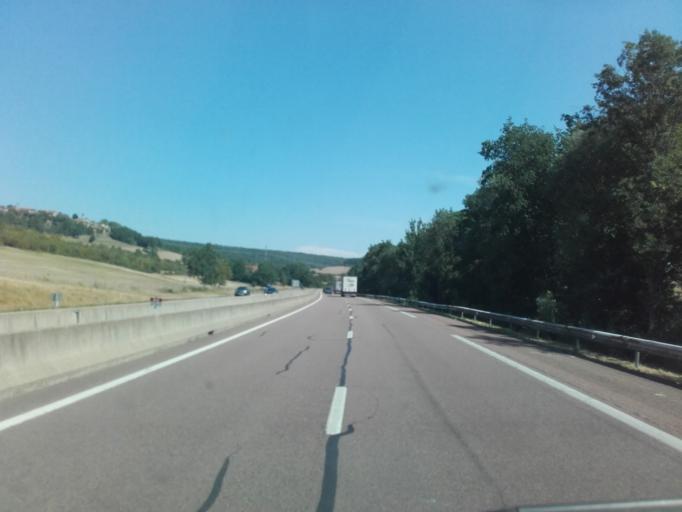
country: FR
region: Bourgogne
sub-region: Departement de la Cote-d'Or
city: Pouilly-en-Auxois
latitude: 47.1997
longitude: 4.6535
